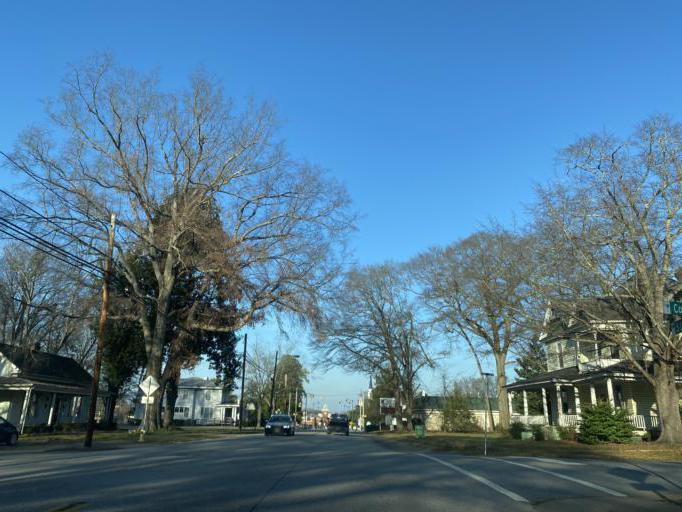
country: US
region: South Carolina
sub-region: Cherokee County
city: Gaffney
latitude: 35.0694
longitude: -81.6523
